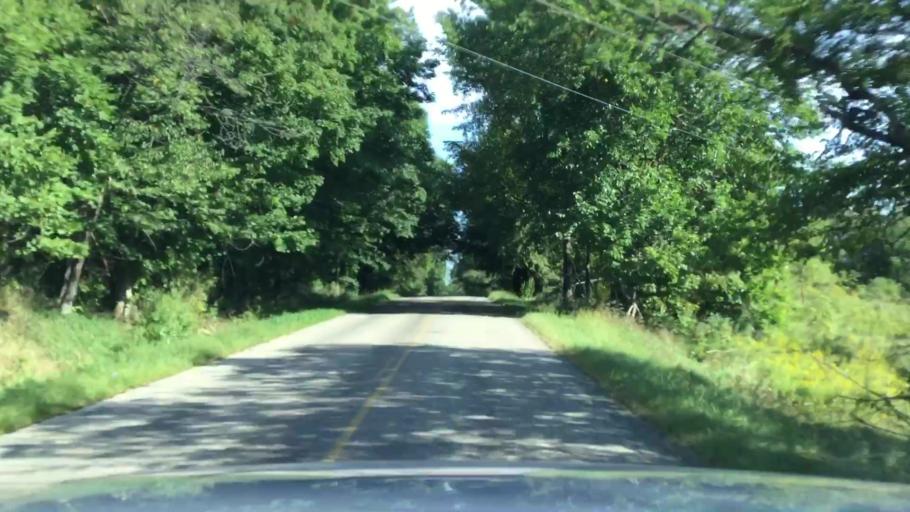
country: US
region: Michigan
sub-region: Lenawee County
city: Hudson
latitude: 41.9084
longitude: -84.4204
